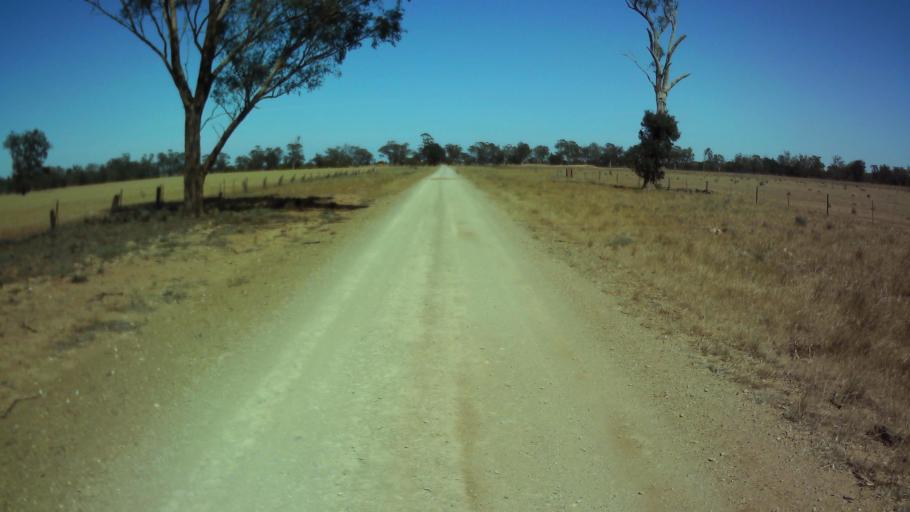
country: AU
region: New South Wales
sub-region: Weddin
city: Grenfell
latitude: -33.8725
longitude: 147.8654
